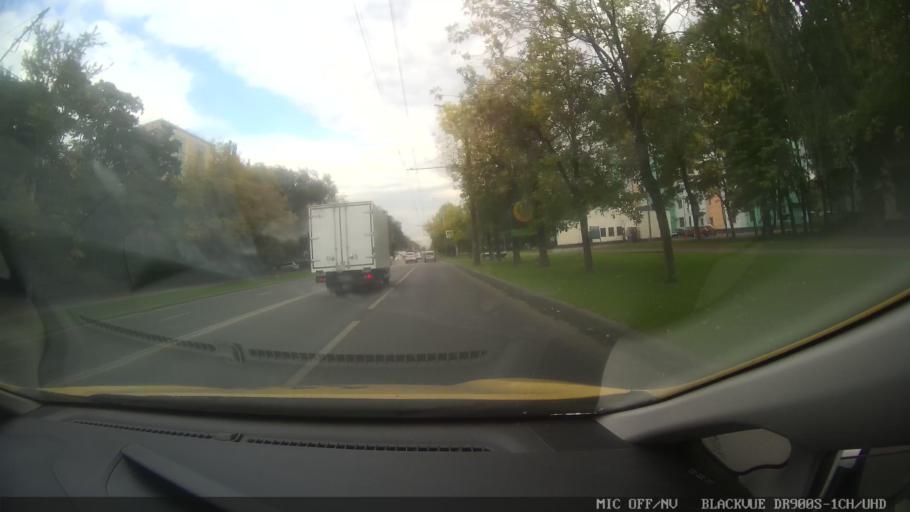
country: RU
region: Moscow
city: Novyye Kuz'minki
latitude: 55.6992
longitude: 37.7696
